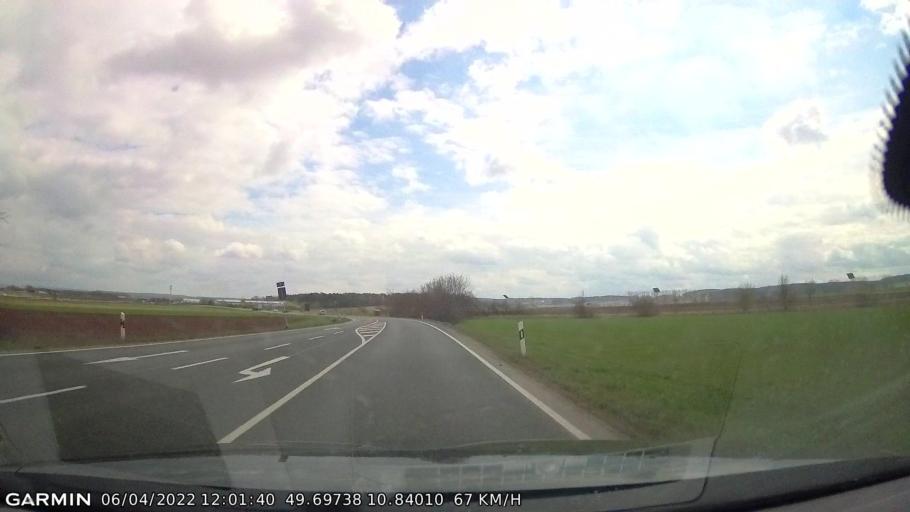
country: DE
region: Bavaria
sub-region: Regierungsbezirk Mittelfranken
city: Gremsdorf
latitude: 49.6972
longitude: 10.8403
